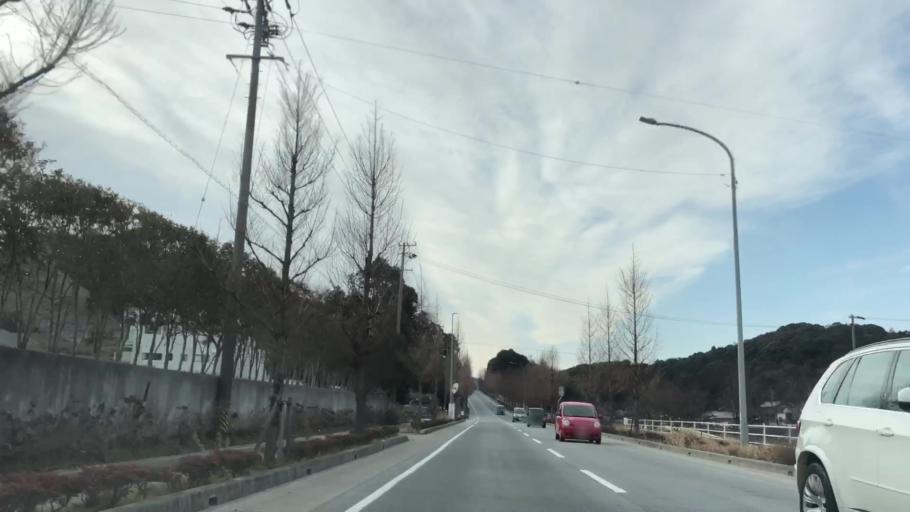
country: JP
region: Aichi
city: Gamagori
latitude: 34.8309
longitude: 137.1714
